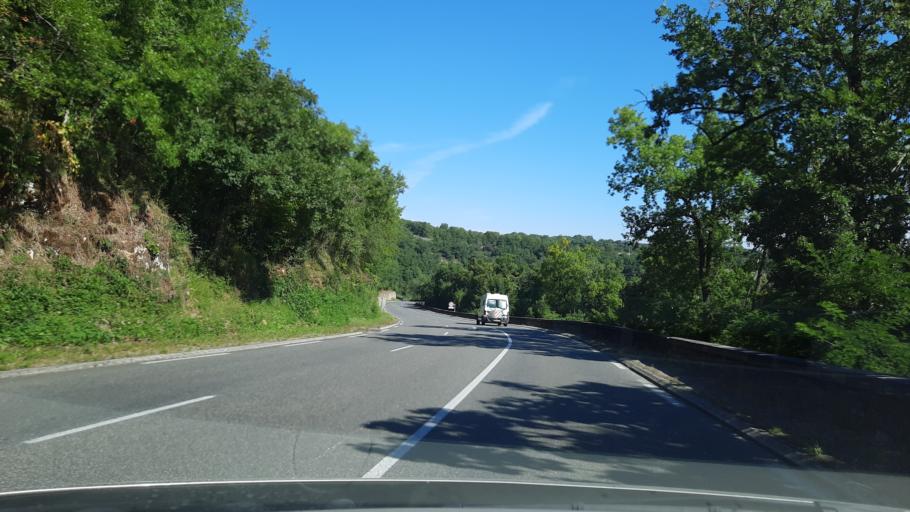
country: FR
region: Midi-Pyrenees
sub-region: Departement du Tarn-et-Garonne
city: Caylus
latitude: 44.2327
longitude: 1.7677
